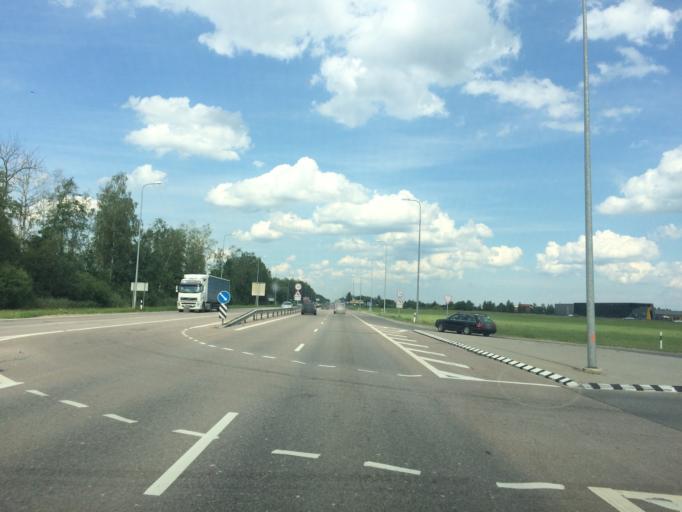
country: LT
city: Ramuciai
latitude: 54.9432
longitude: 24.0054
